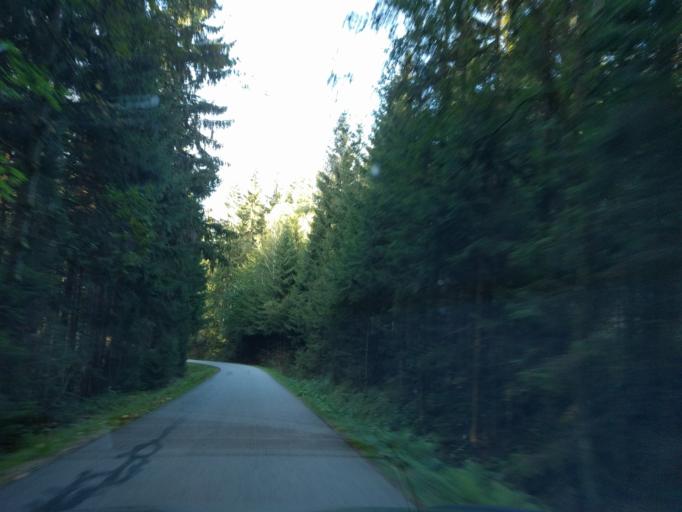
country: DE
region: Bavaria
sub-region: Upper Palatinate
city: Hohenwarth
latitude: 49.1881
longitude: 12.9346
